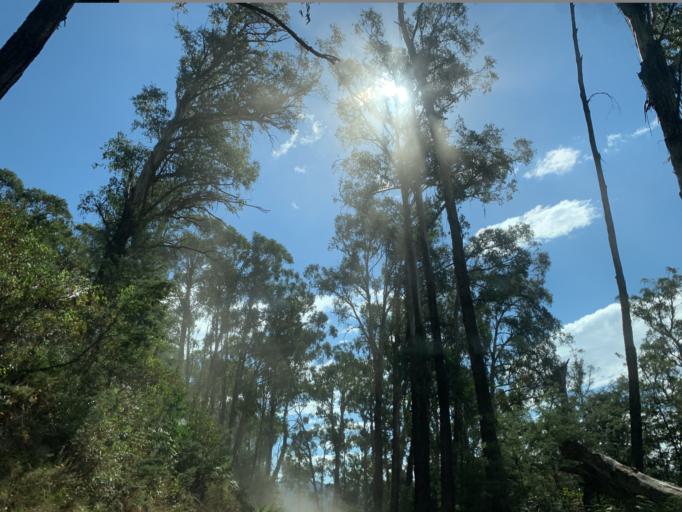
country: AU
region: Victoria
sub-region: Mansfield
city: Mansfield
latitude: -37.0982
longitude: 146.4867
